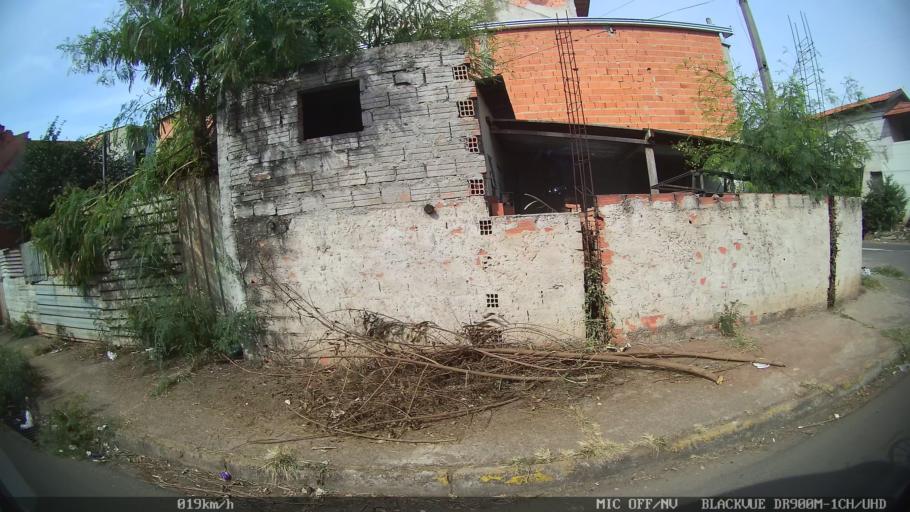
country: BR
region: Sao Paulo
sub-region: Piracicaba
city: Piracicaba
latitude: -22.7460
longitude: -47.6565
